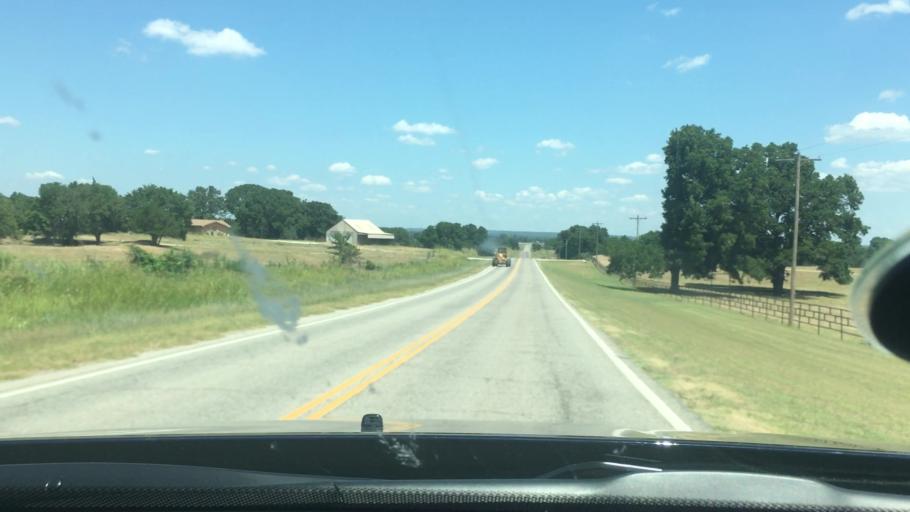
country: US
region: Oklahoma
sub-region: Carter County
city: Dickson
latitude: 34.2066
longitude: -96.9771
